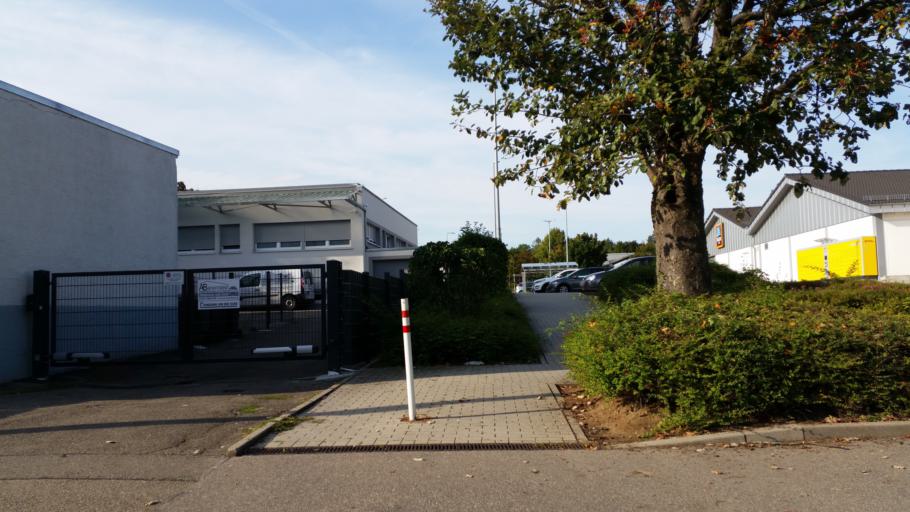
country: DE
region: Baden-Wuerttemberg
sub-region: Regierungsbezirk Stuttgart
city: Ludwigsburg
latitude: 48.8793
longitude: 9.2185
